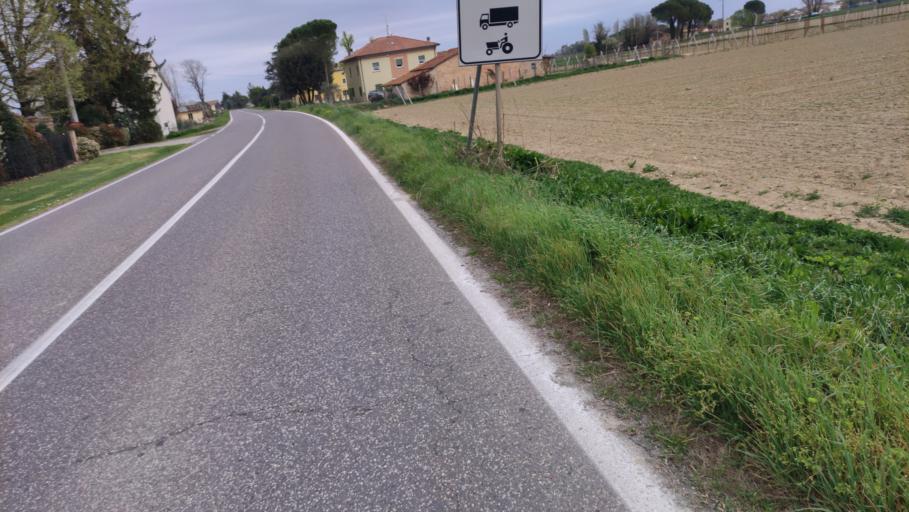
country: IT
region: Emilia-Romagna
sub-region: Provincia di Ravenna
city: Godo
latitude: 44.3916
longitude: 12.0528
